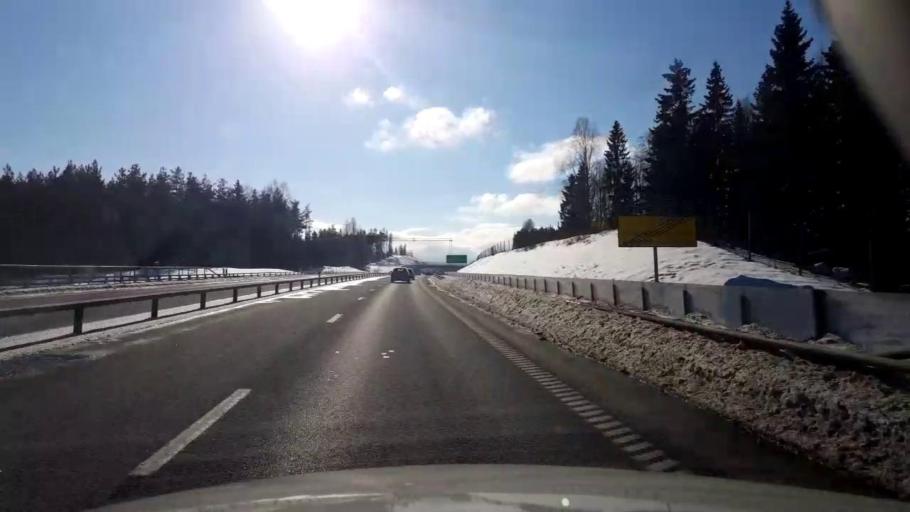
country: SE
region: Vaesternorrland
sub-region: Sundsvalls Kommun
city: Nolby
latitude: 62.2886
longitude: 17.3491
